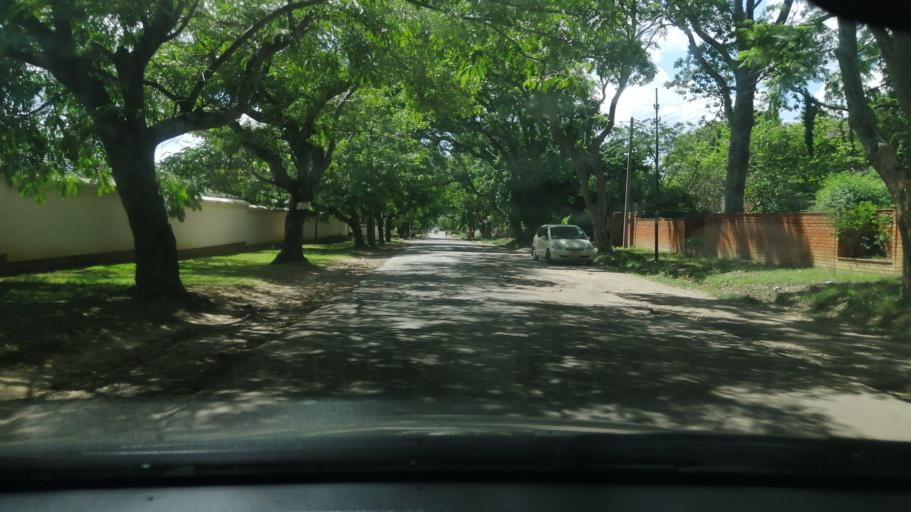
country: ZW
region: Harare
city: Harare
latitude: -17.8118
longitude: 31.0780
